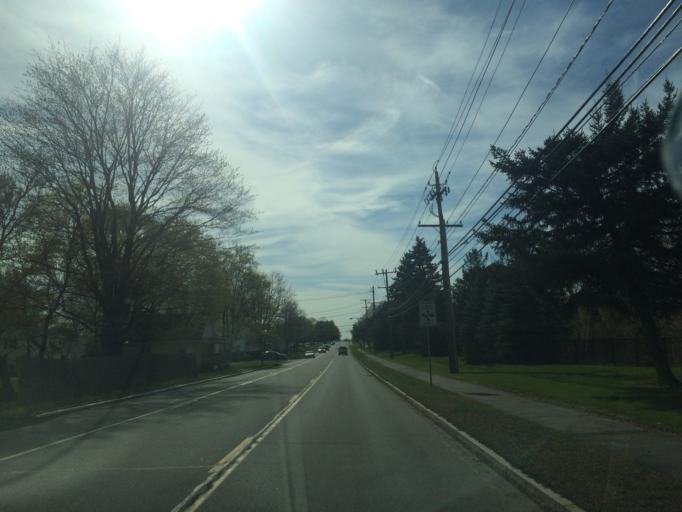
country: US
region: New York
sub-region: Monroe County
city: Fairport
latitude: 43.1085
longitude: -77.4451
